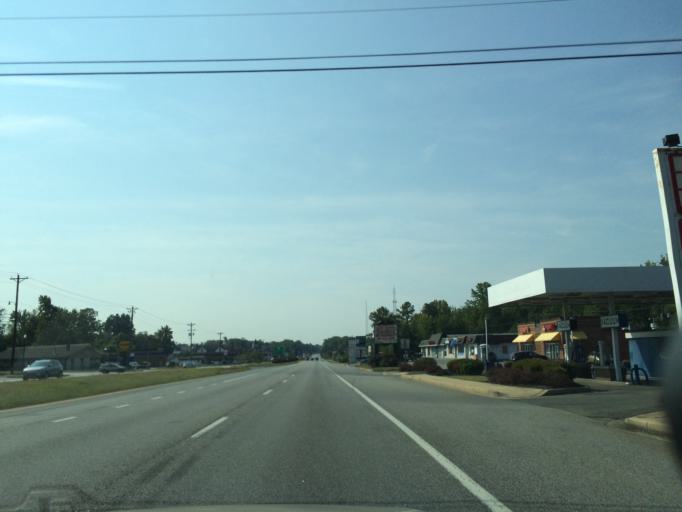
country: US
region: Maryland
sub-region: Charles County
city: La Plata
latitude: 38.5339
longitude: -76.9836
